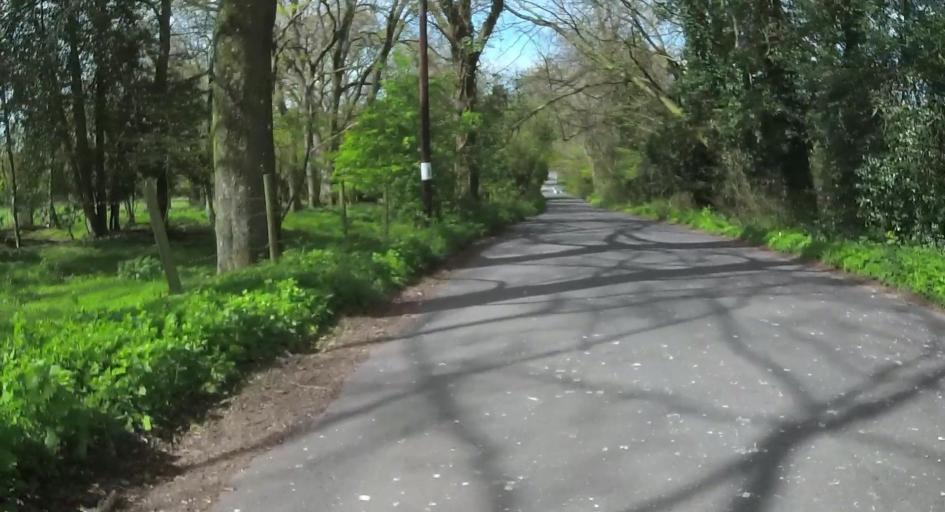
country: GB
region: England
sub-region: Hampshire
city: Chandlers Ford
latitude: 51.0607
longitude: -1.3789
